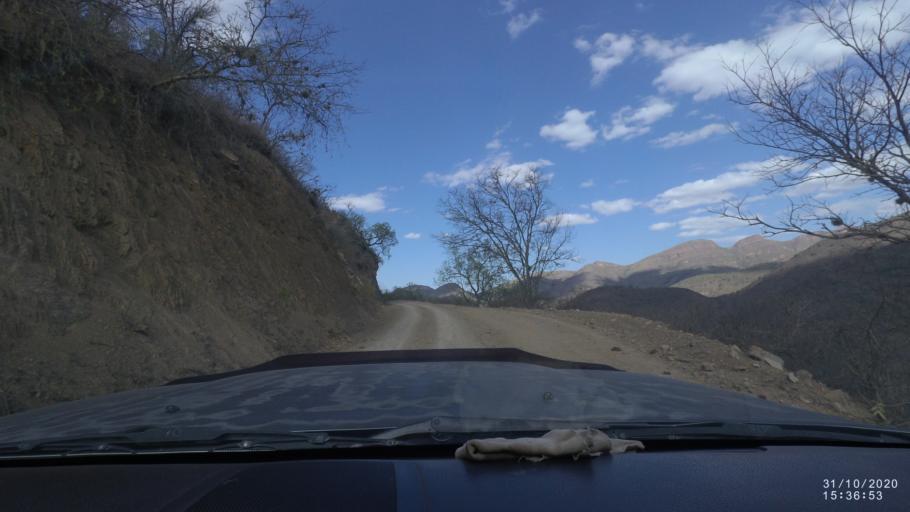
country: BO
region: Chuquisaca
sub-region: Provincia Zudanez
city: Mojocoya
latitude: -18.3405
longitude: -64.7513
